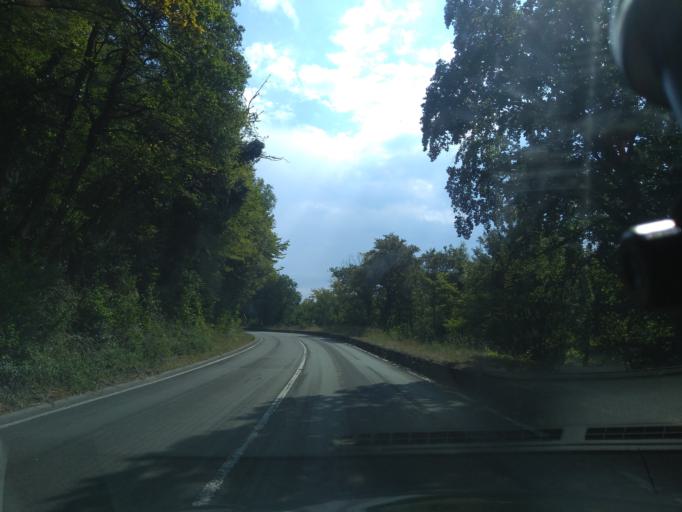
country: BE
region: Wallonia
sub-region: Province de Namur
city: Dinant
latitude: 50.2322
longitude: 4.8907
